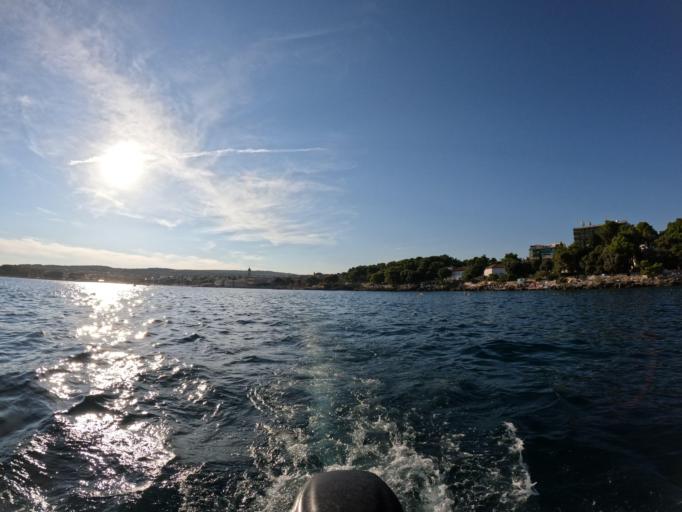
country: HR
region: Primorsko-Goranska
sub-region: Grad Krk
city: Krk
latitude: 45.0234
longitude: 14.5824
